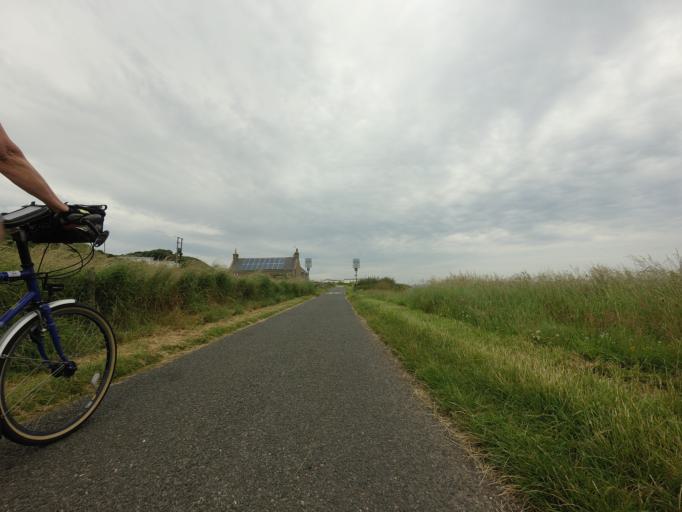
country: GB
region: Scotland
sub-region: Aberdeenshire
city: Whitehills
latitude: 57.6796
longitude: -2.5690
